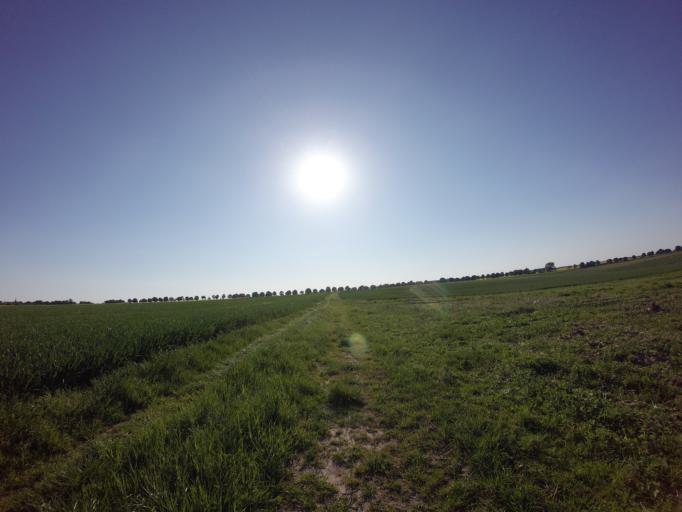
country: PL
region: West Pomeranian Voivodeship
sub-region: Powiat choszczenski
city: Choszczno
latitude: 53.1429
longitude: 15.3889
